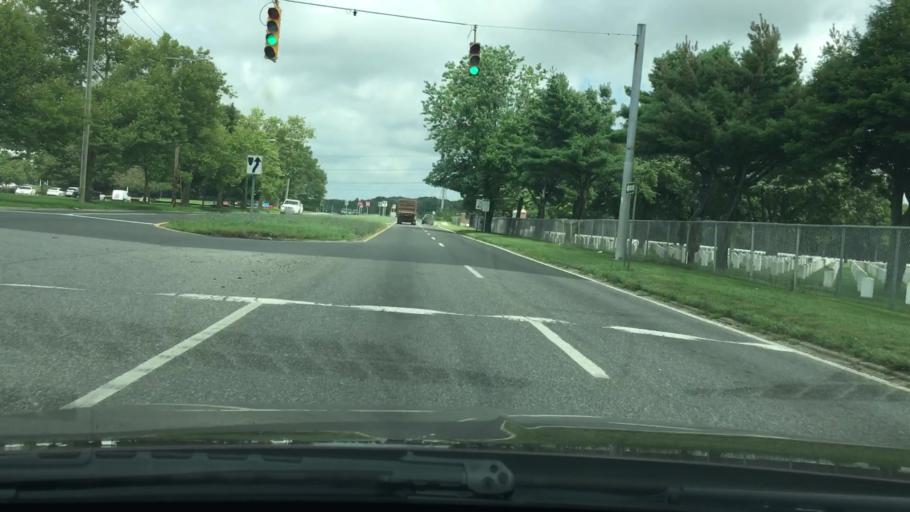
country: US
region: New York
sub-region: Suffolk County
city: Wheatley Heights
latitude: 40.7611
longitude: -73.4032
